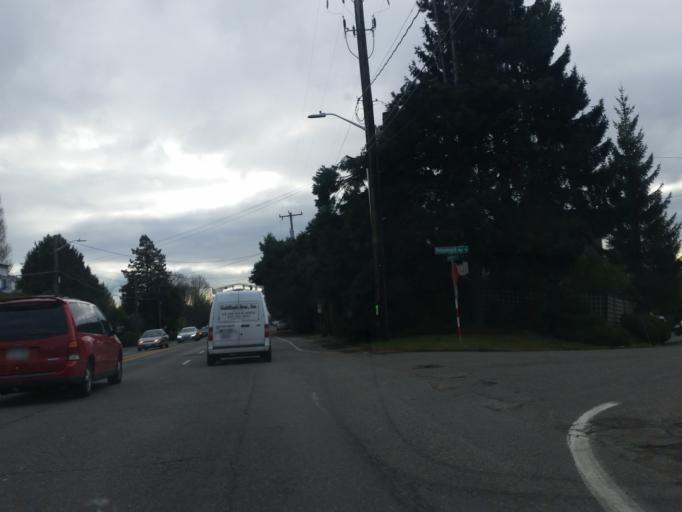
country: US
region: Washington
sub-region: King County
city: Shoreline
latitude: 47.7193
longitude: -122.3556
